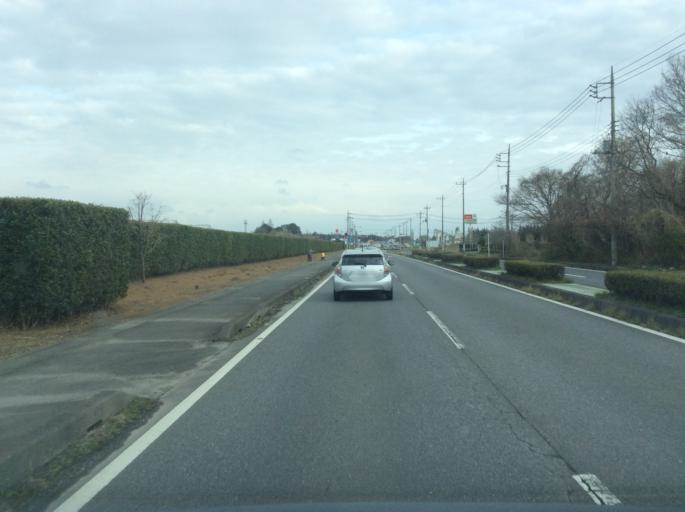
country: JP
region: Ibaraki
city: Naka
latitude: 36.1233
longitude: 140.1743
